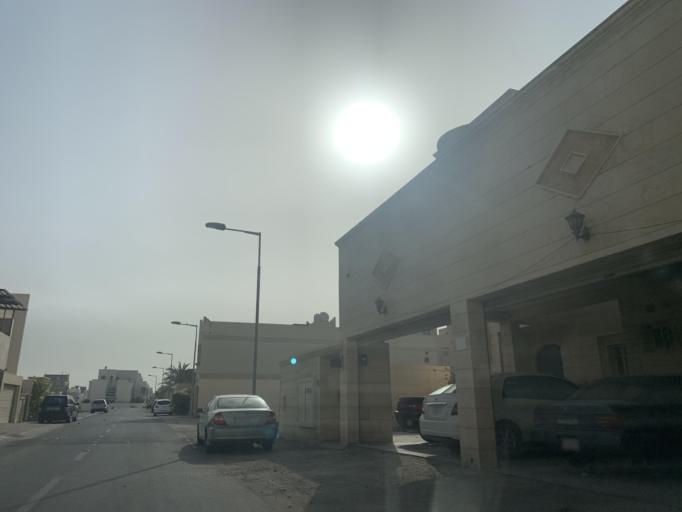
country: BH
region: Northern
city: Madinat `Isa
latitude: 26.1886
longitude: 50.5579
